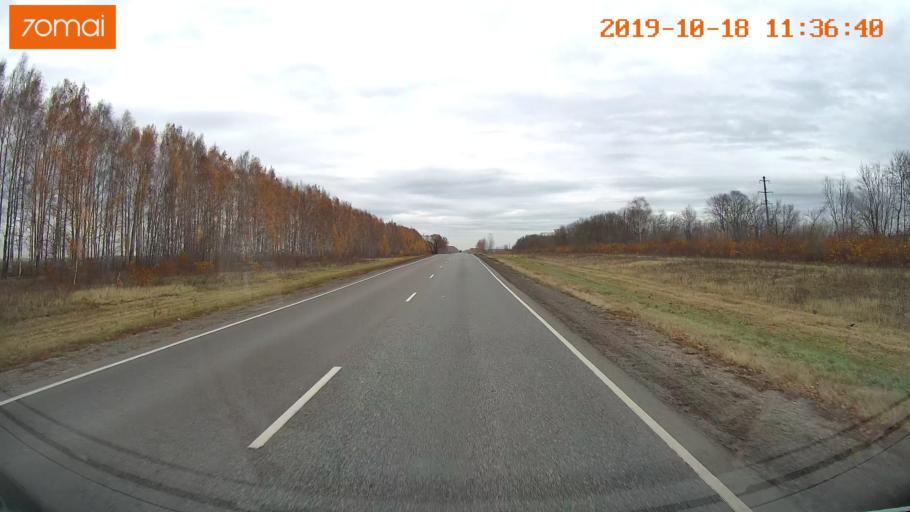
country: RU
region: Rjazan
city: Oktyabr'skiy
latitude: 54.1433
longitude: 38.8122
